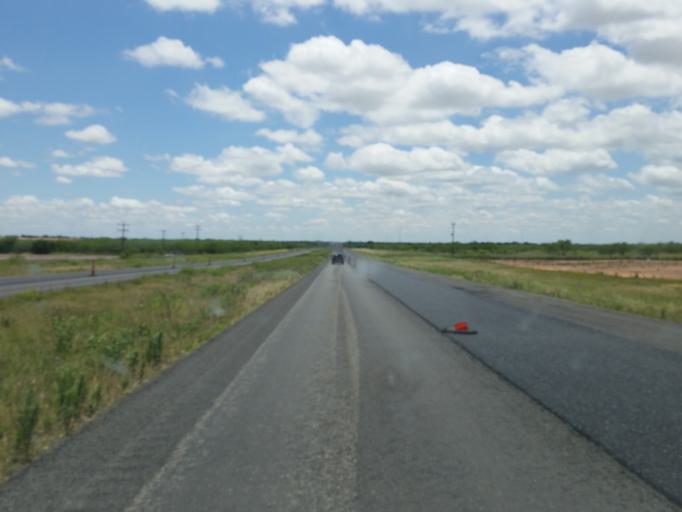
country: US
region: Texas
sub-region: Scurry County
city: Snyder
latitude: 32.7725
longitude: -100.9396
